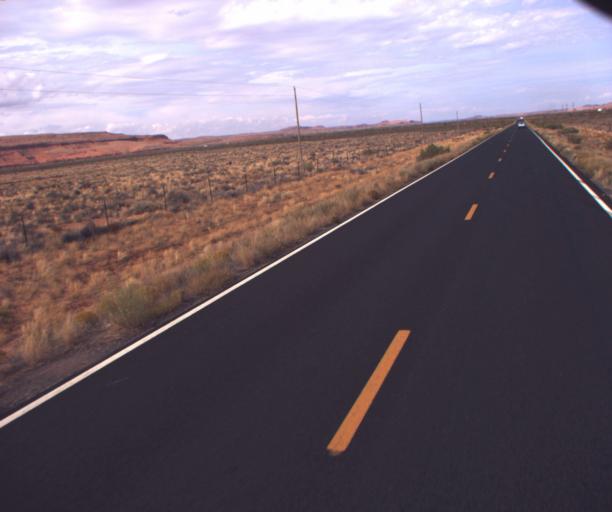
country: US
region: Arizona
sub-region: Apache County
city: Many Farms
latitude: 36.6188
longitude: -109.5809
